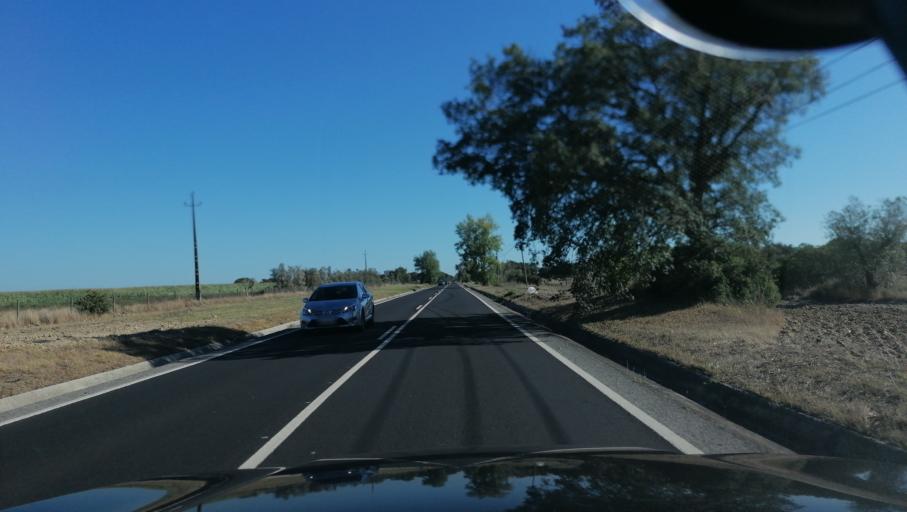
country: PT
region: Santarem
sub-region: Benavente
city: Poceirao
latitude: 38.8238
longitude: -8.8809
